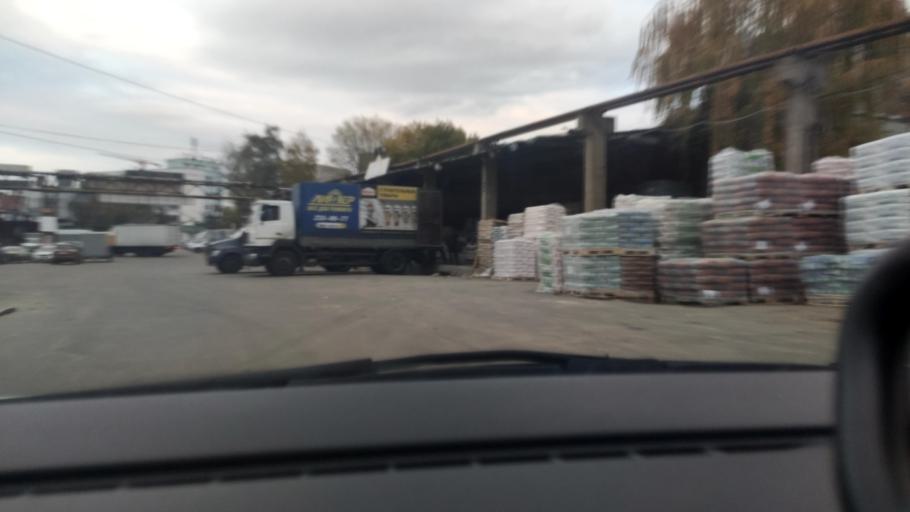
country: RU
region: Voronezj
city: Voronezh
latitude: 51.6645
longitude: 39.1576
